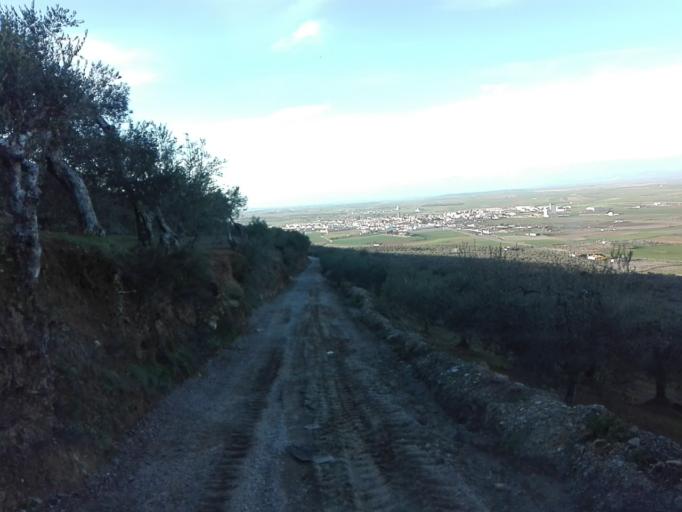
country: ES
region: Extremadura
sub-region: Provincia de Badajoz
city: Llerena
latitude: 38.2157
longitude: -6.0002
